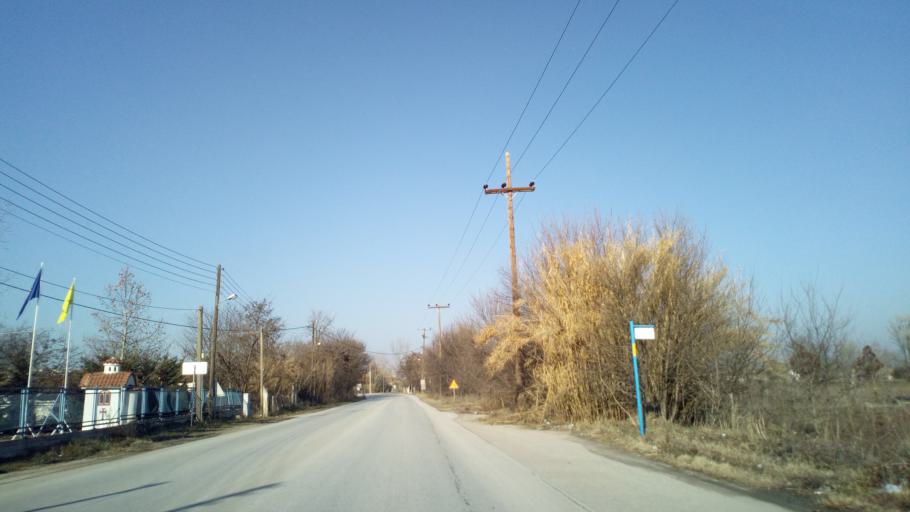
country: GR
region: Central Macedonia
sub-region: Nomos Thessalonikis
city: Lagkadas
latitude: 40.7463
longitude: 23.0778
